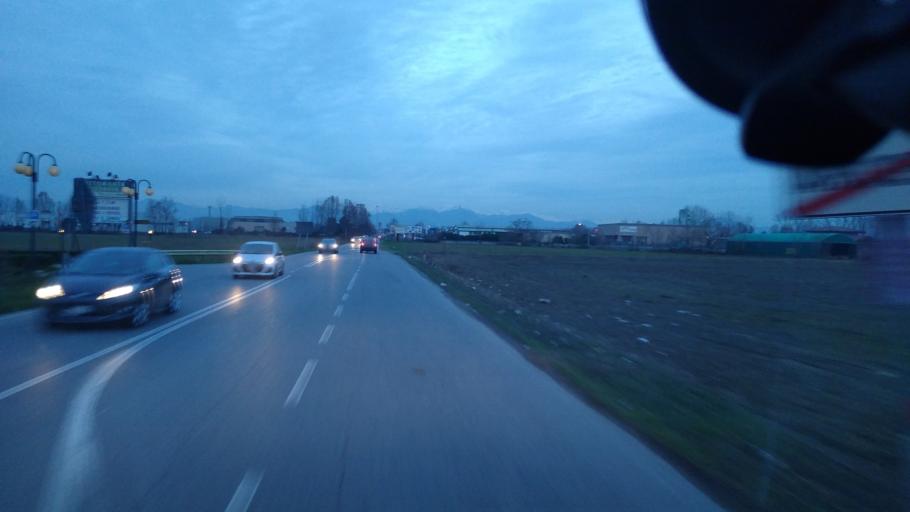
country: IT
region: Lombardy
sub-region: Provincia di Bergamo
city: Arcene
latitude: 45.5854
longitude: 9.6183
